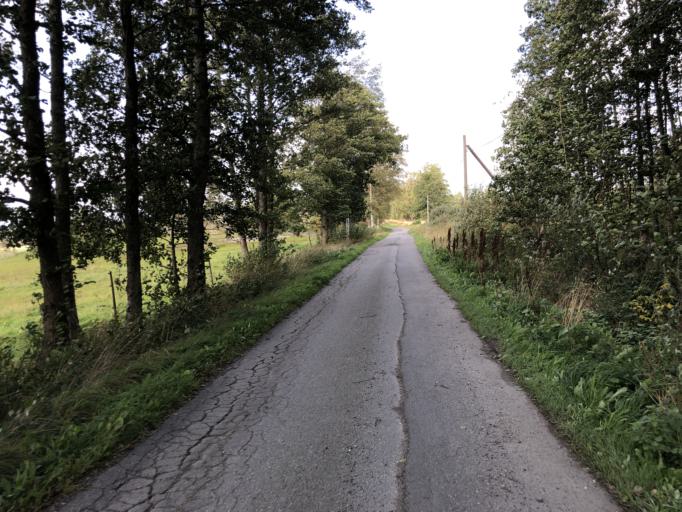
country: SE
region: Vaestra Goetaland
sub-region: Goteborg
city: Majorna
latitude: 57.7498
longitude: 11.8616
